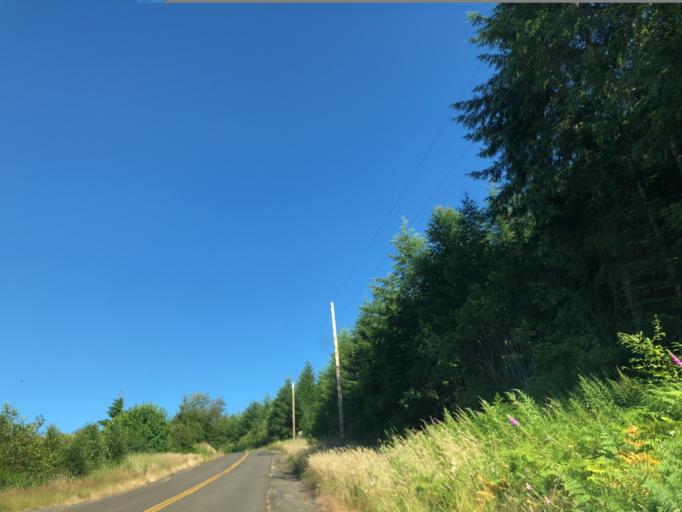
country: US
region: Oregon
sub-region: Linn County
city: Sweet Home
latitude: 44.4646
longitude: -122.6709
